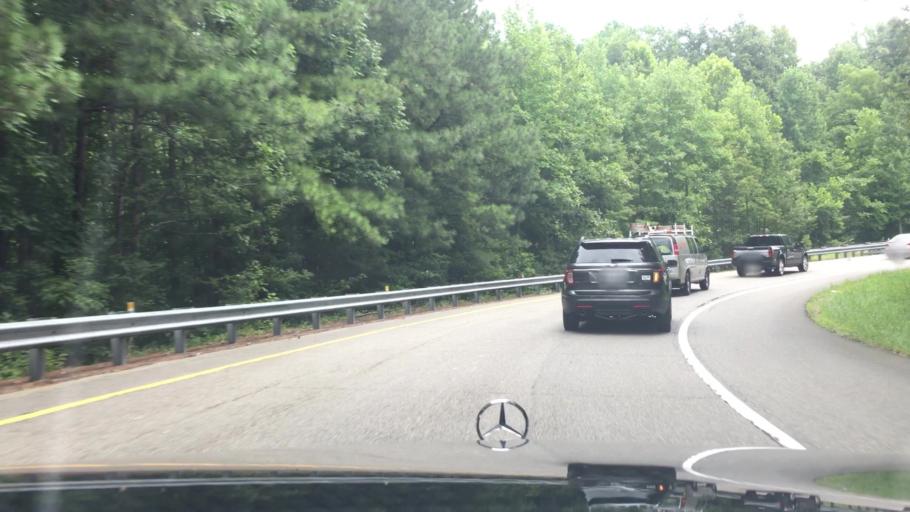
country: US
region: Virginia
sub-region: Chesterfield County
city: Brandermill
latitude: 37.4239
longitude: -77.6286
